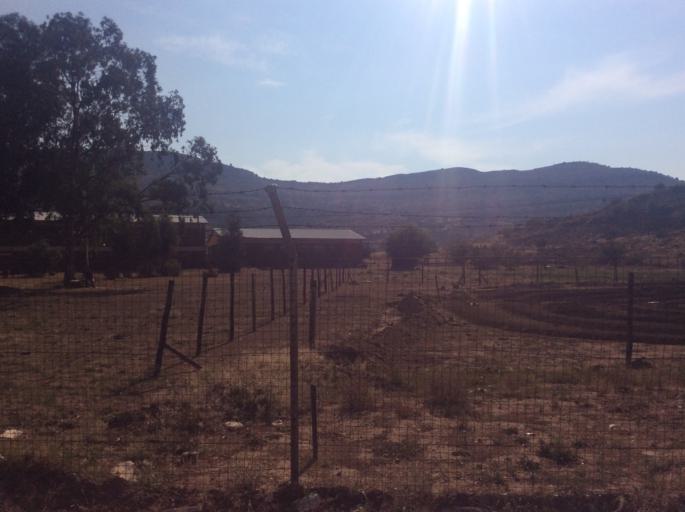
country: LS
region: Mafeteng
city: Mafeteng
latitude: -29.7174
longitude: 27.0317
